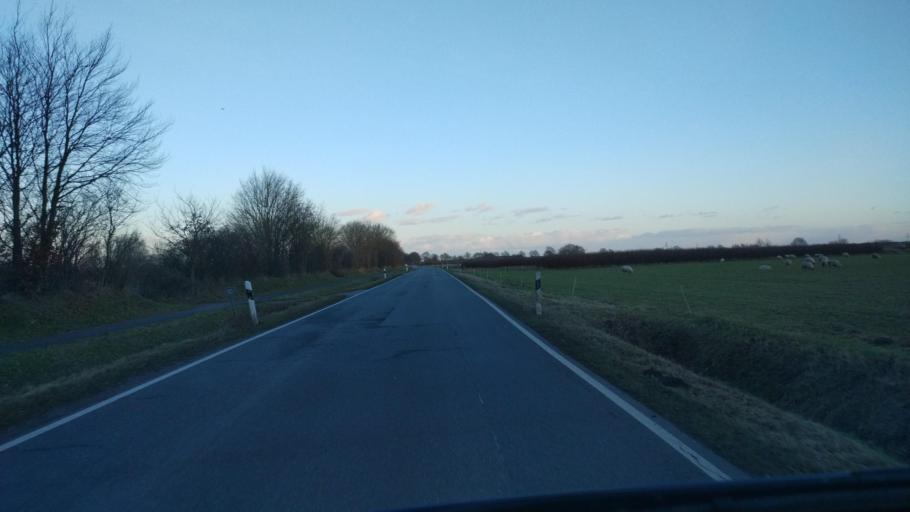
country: DE
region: Schleswig-Holstein
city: Ellingstedt
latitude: 54.4656
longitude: 9.3781
